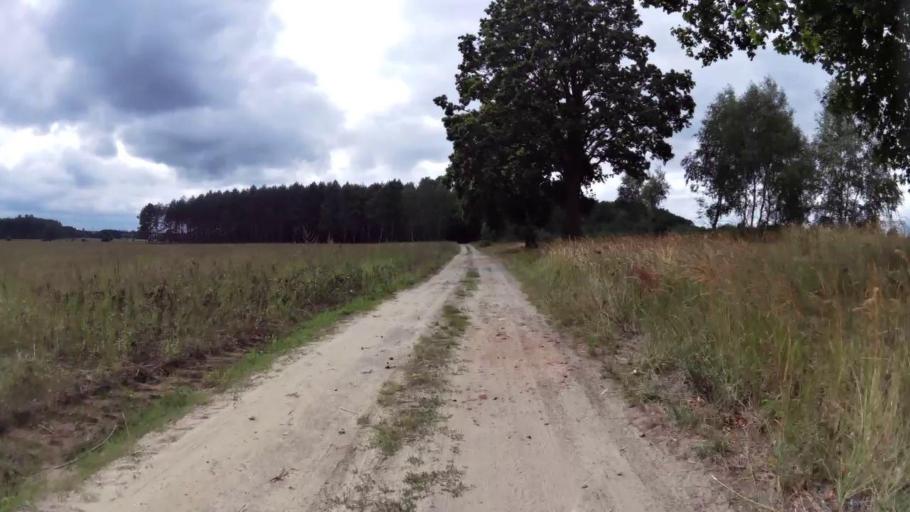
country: PL
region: West Pomeranian Voivodeship
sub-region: Powiat mysliborski
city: Debno
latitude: 52.7623
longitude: 14.7108
